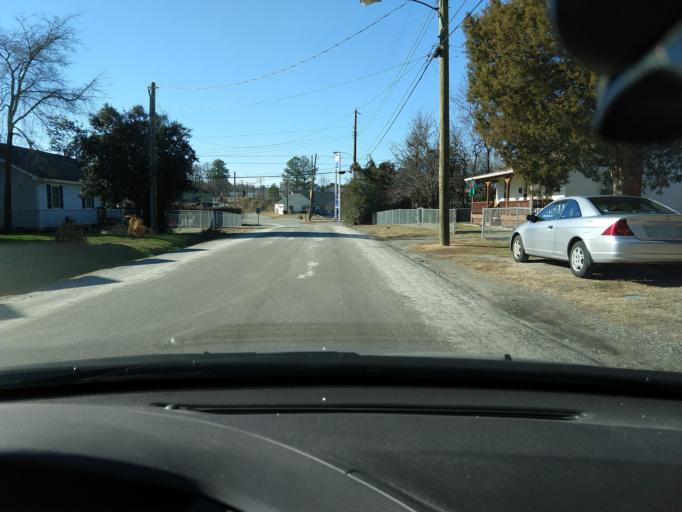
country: US
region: Virginia
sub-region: Chesterfield County
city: Bensley
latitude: 37.4663
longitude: -77.4418
